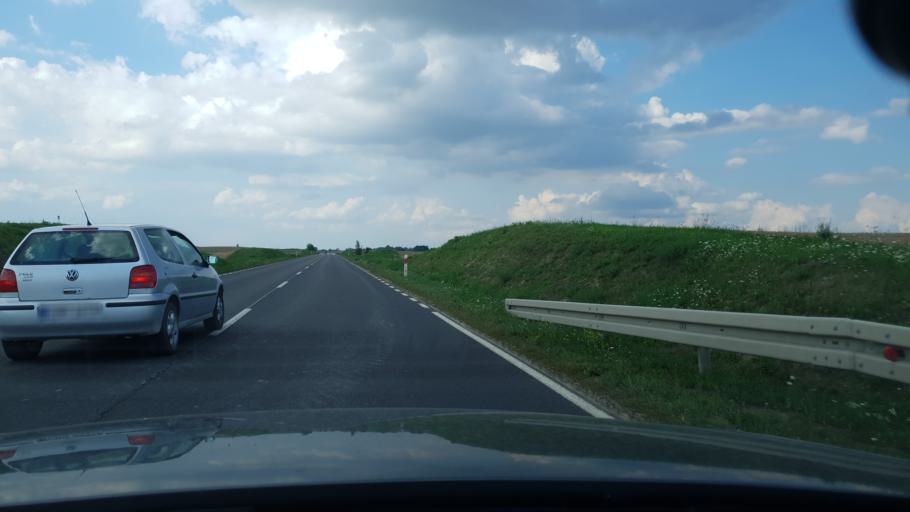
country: PL
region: Kujawsko-Pomorskie
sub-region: Powiat wabrzeski
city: Wabrzezno
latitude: 53.2955
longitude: 18.9259
